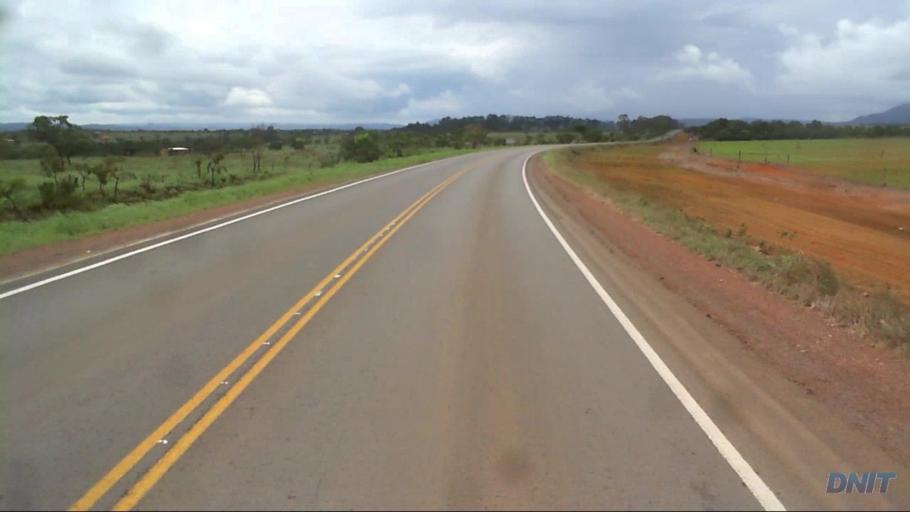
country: BR
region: Goias
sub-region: Padre Bernardo
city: Padre Bernardo
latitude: -15.3080
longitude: -48.2270
